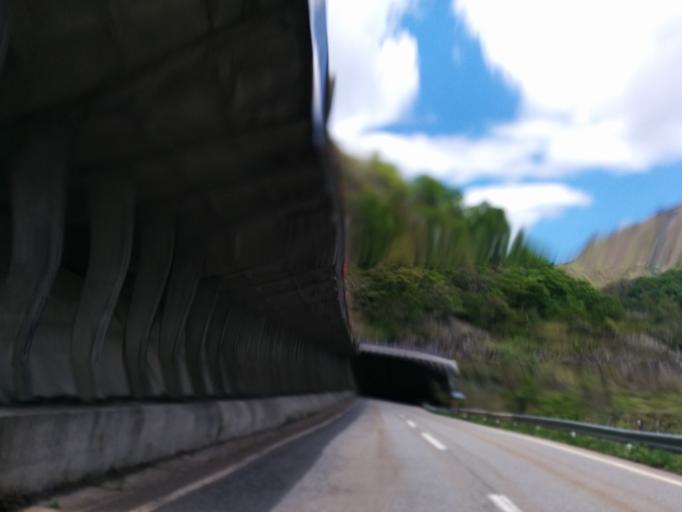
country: JP
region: Toyama
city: Fukumitsu
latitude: 36.3161
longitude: 136.8995
